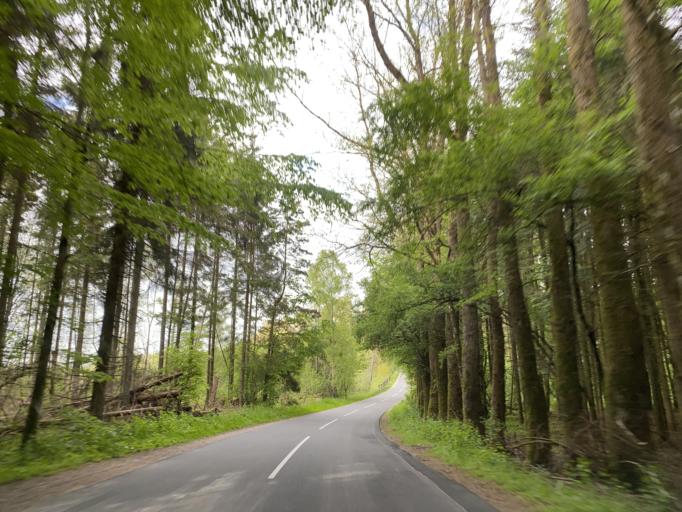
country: DK
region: Central Jutland
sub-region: Horsens Kommune
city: Braedstrup
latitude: 56.0323
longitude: 9.6565
